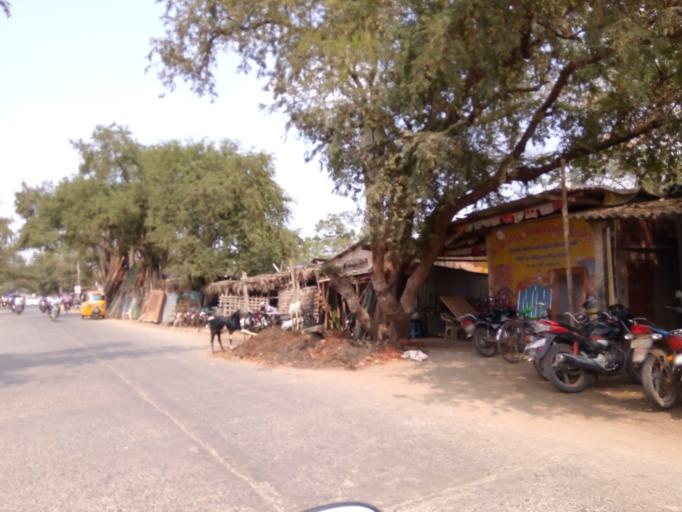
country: IN
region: Andhra Pradesh
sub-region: Prakasam
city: pedda nakkalapalem
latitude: 15.9650
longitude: 80.2780
